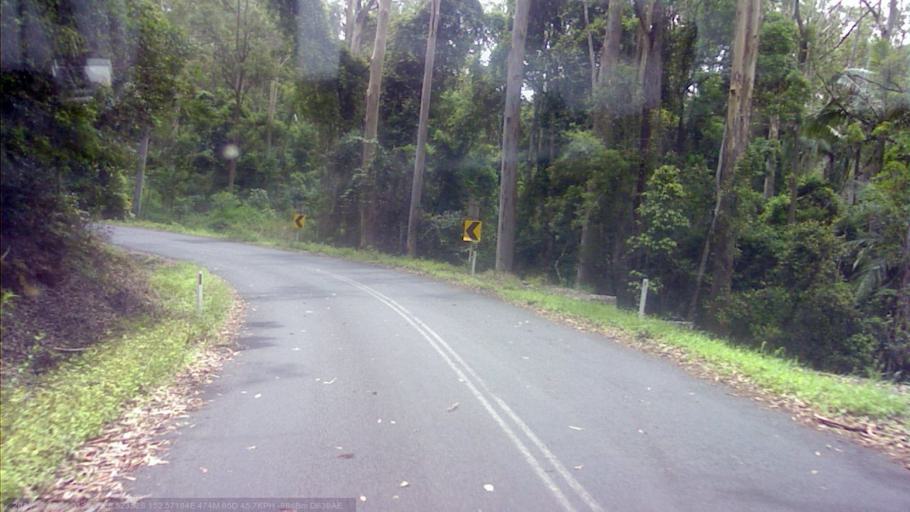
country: AU
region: New South Wales
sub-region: Kyogle
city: Kyogle
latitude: -28.5235
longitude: 152.5718
